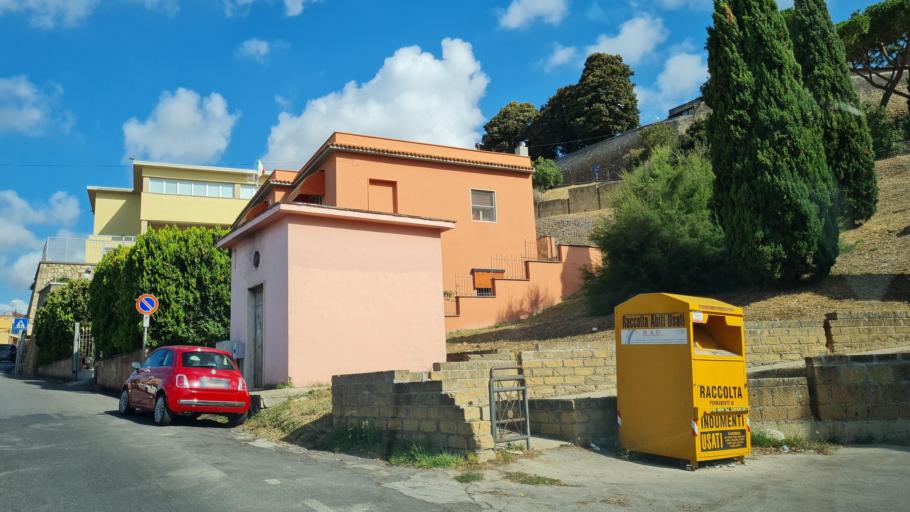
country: IT
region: Latium
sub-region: Provincia di Viterbo
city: Tarquinia
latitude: 42.2503
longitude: 11.7540
